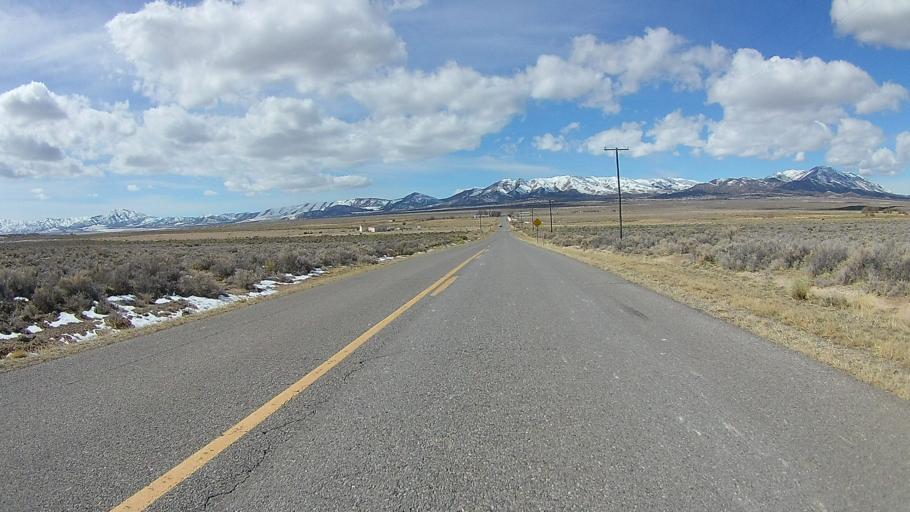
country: US
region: Utah
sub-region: Tooele County
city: Tooele
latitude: 40.1738
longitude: -112.4135
